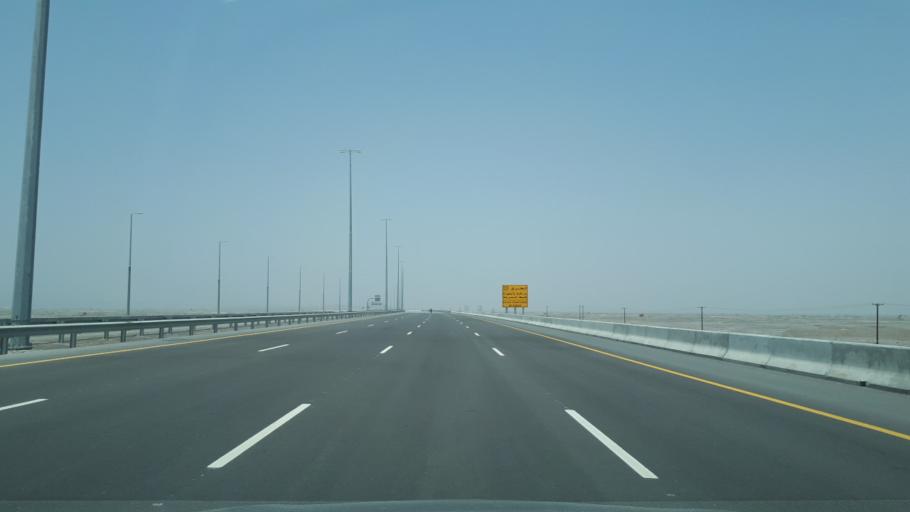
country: OM
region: Al Batinah
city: Barka'
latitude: 23.5723
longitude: 57.7178
